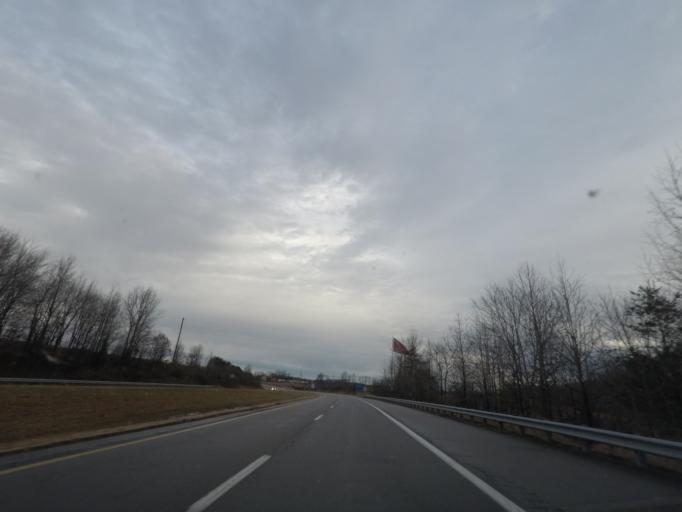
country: US
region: Virginia
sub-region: Pittsylvania County
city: Mount Hermon
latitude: 36.6878
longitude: -79.3617
